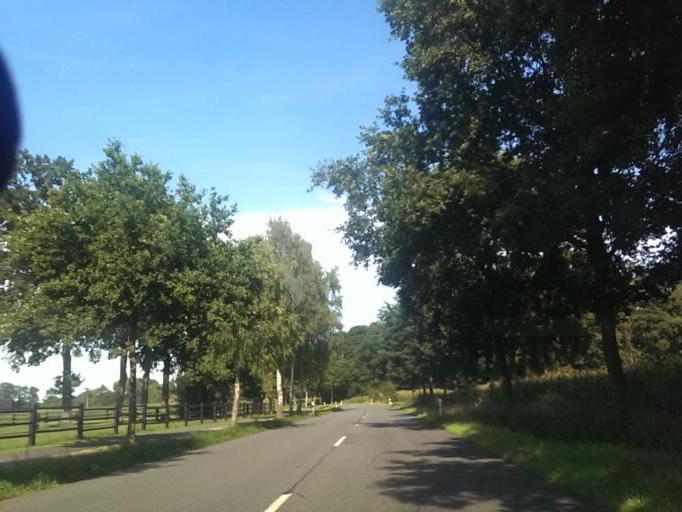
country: DE
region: North Rhine-Westphalia
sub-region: Regierungsbezirk Detmold
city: Hovelhof
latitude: 51.7963
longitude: 8.6625
